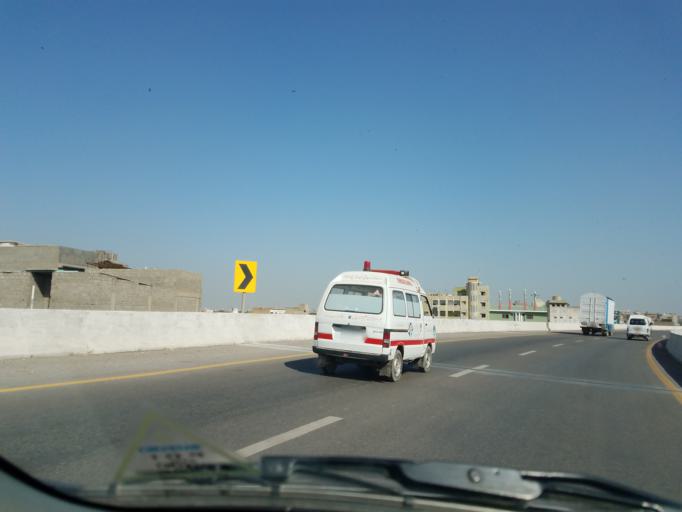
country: PK
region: Sindh
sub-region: Karachi District
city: Karachi
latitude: 24.8825
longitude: 67.0046
